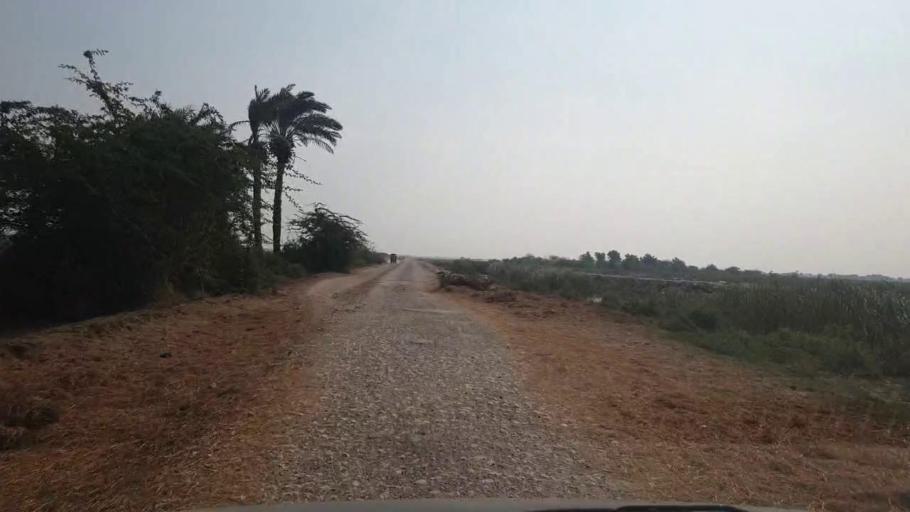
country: PK
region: Sindh
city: Tando Muhammad Khan
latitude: 25.0944
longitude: 68.3813
